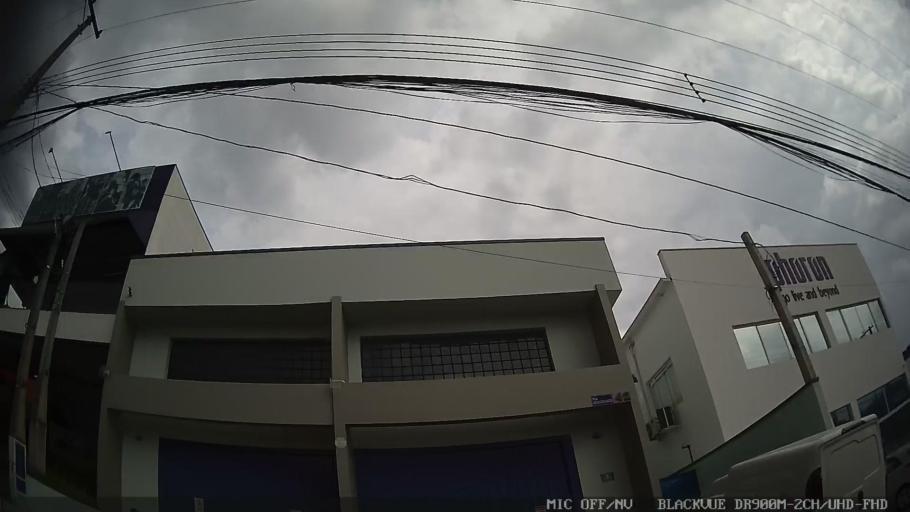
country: BR
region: Sao Paulo
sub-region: Vinhedo
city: Vinhedo
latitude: -23.0350
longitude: -46.9762
